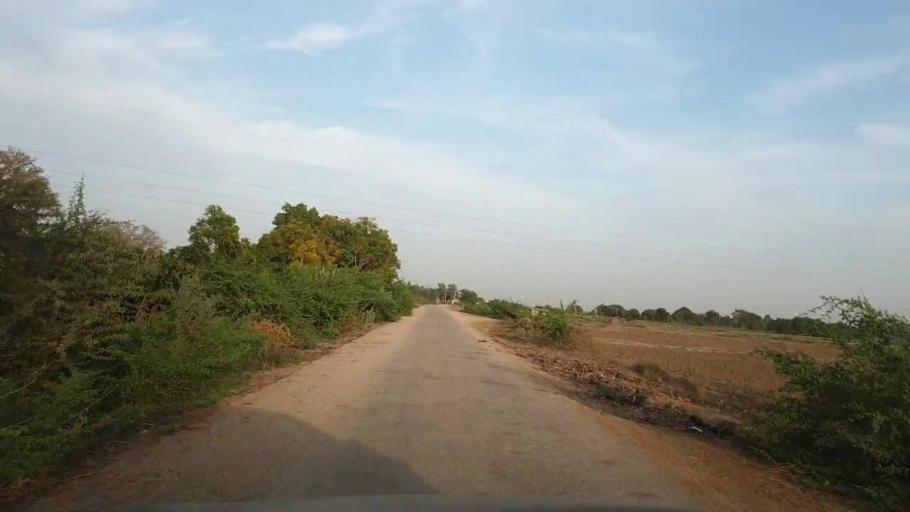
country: PK
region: Sindh
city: Kunri
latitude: 25.1601
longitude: 69.5504
